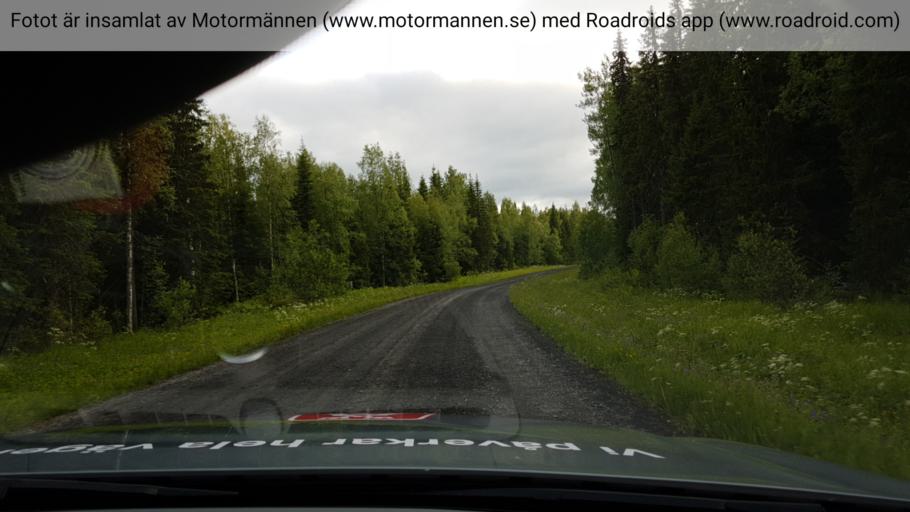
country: SE
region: Jaemtland
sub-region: OEstersunds Kommun
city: Lit
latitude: 63.6387
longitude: 15.0715
